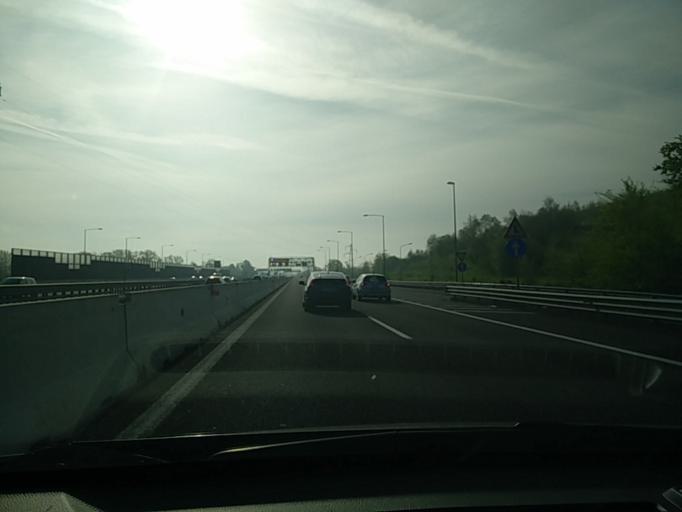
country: IT
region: Emilia-Romagna
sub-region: Provincia di Bologna
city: San Lazzaro
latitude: 44.4843
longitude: 11.4106
